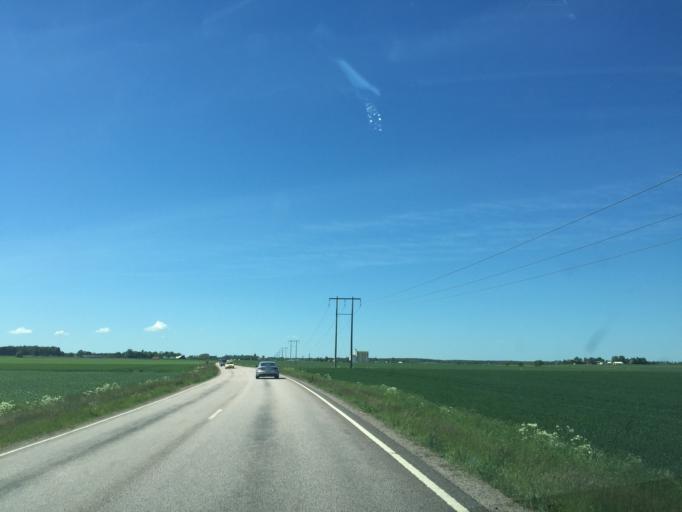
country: SE
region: OEstergoetland
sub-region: Mjolby Kommun
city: Mjolby
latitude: 58.3865
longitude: 15.1387
